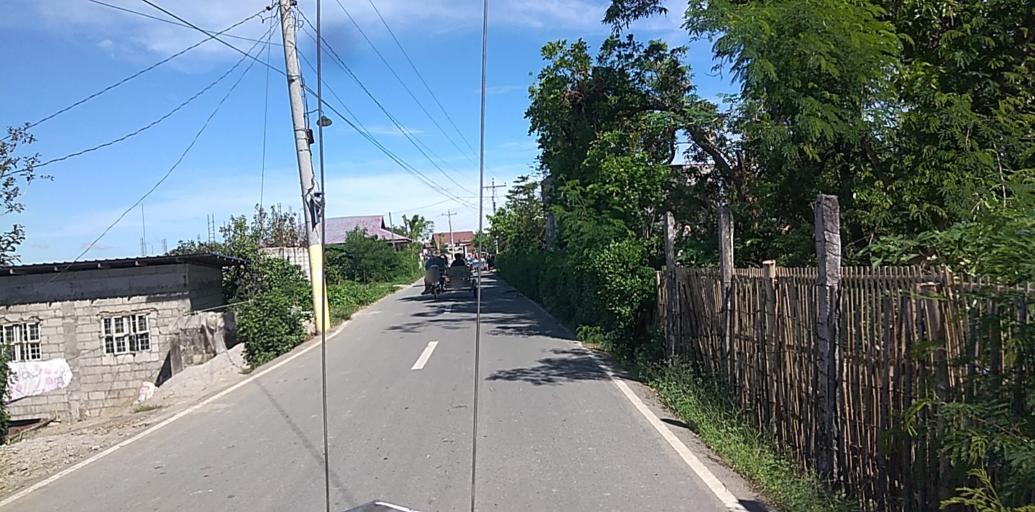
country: PH
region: Central Luzon
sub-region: Province of Pampanga
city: Candaba
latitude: 15.1081
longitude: 120.8165
